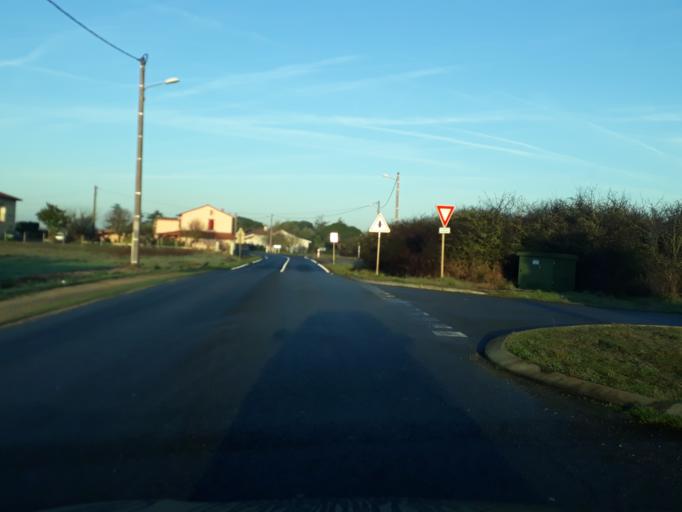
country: FR
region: Midi-Pyrenees
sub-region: Departement de la Haute-Garonne
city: Longages
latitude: 43.3574
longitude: 1.2299
